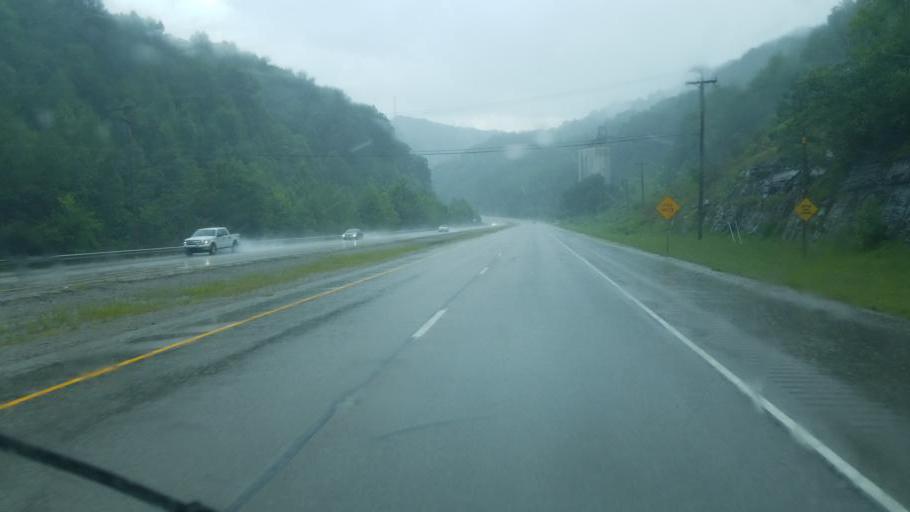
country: US
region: West Virginia
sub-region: Mingo County
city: Williamson
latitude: 37.6050
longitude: -82.3682
